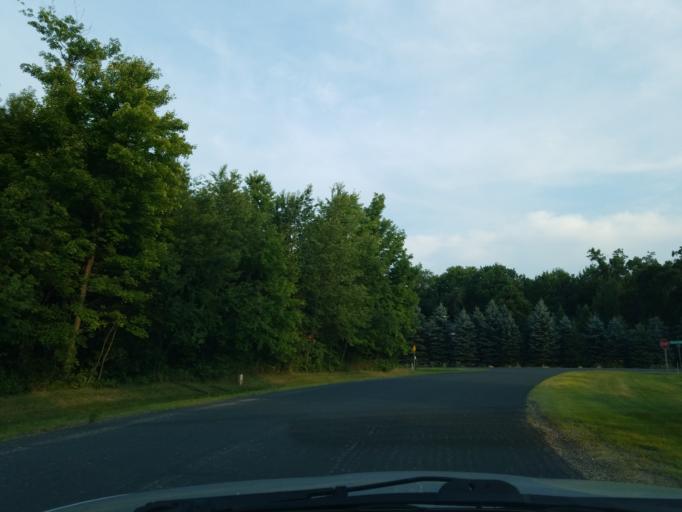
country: US
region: Minnesota
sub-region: Washington County
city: Stillwater
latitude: 45.0670
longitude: -92.7729
